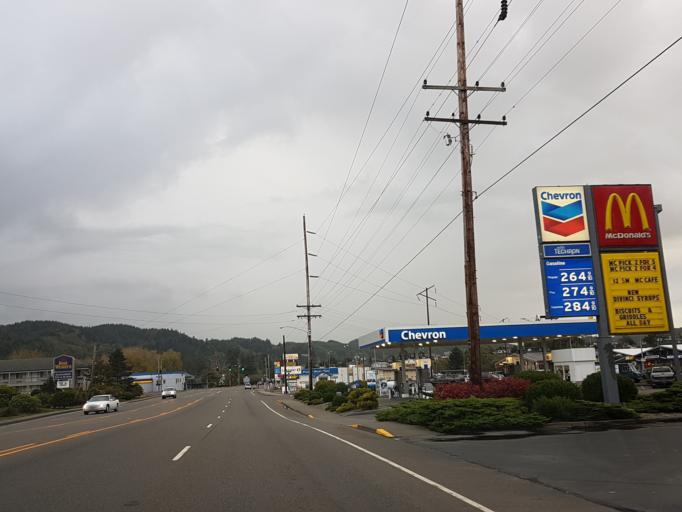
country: US
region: Oregon
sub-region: Douglas County
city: Reedsport
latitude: 43.7000
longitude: -124.1097
